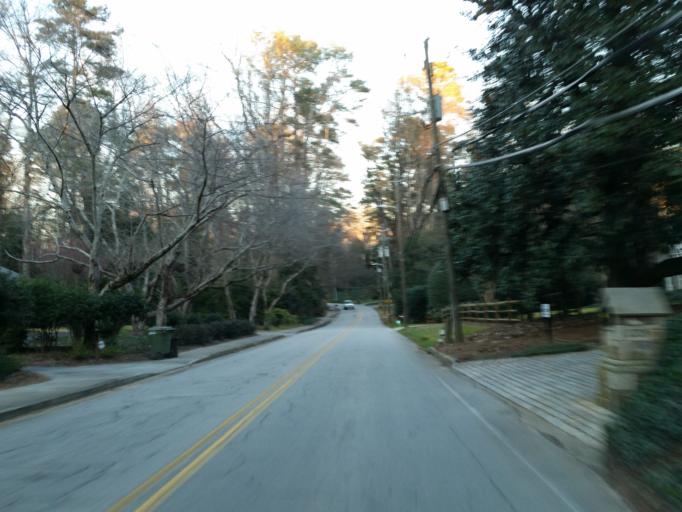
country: US
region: Georgia
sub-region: Cobb County
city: Vinings
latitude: 33.8314
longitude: -84.4310
